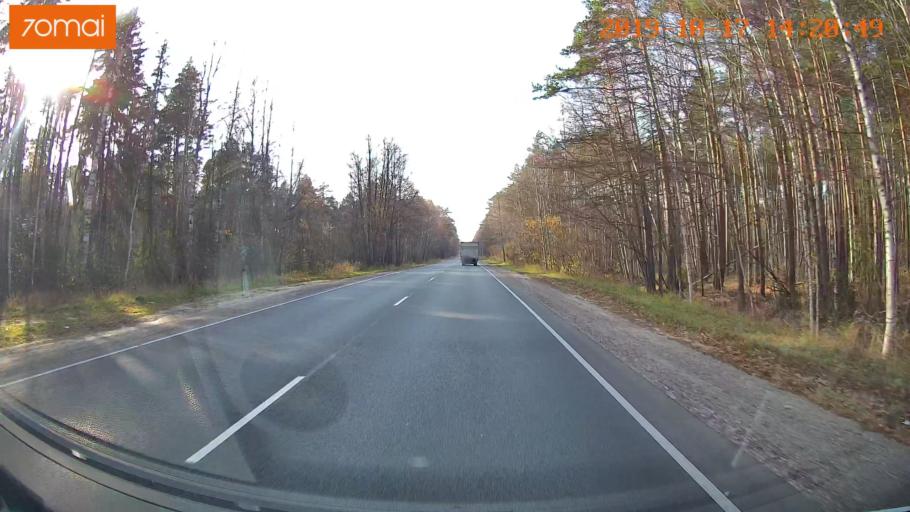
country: RU
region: Rjazan
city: Spas-Klepiki
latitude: 55.0392
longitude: 39.9947
